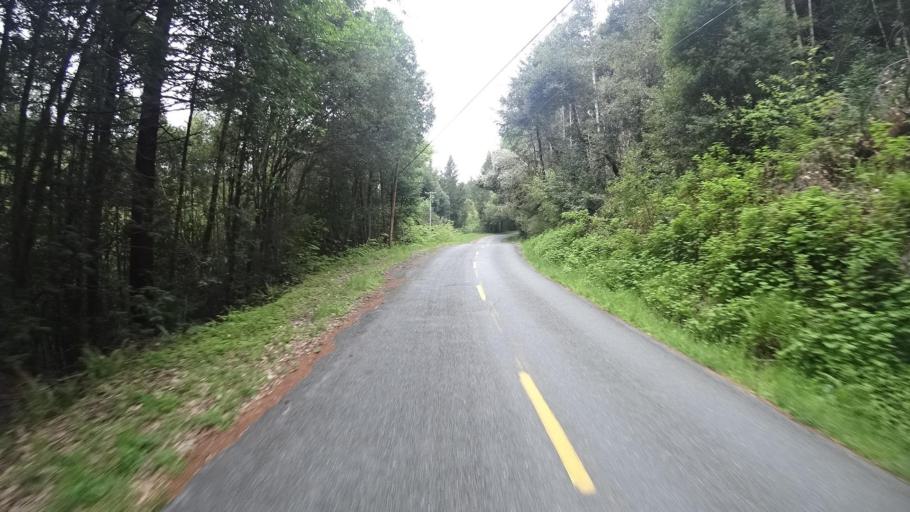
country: US
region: California
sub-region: Humboldt County
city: Blue Lake
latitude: 40.9570
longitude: -123.8376
